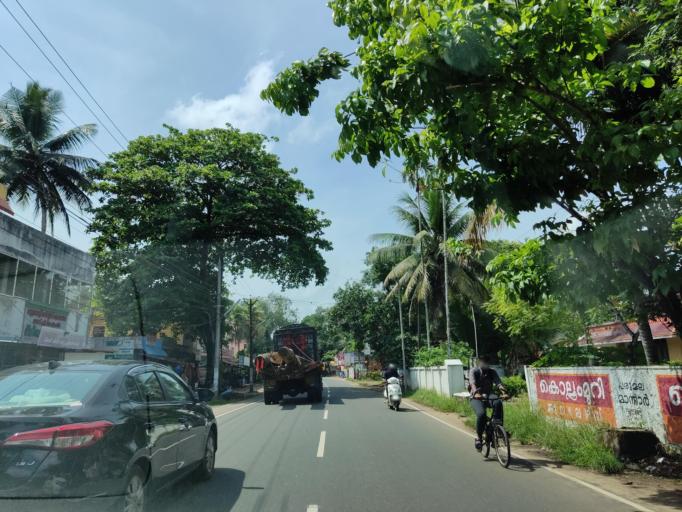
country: IN
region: Kerala
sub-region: Alappuzha
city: Mavelikara
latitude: 9.2987
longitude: 76.5335
